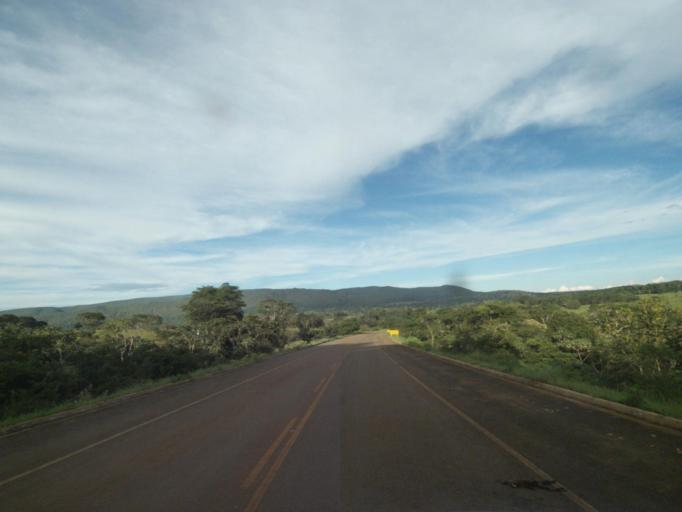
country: BR
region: Goias
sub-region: Jaragua
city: Jaragua
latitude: -15.8446
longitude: -49.3649
